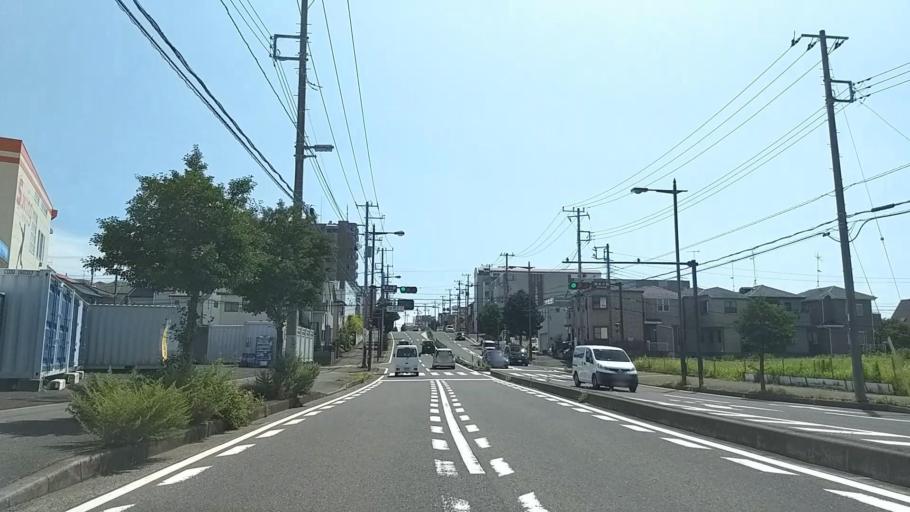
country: JP
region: Kanagawa
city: Fujisawa
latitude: 35.3563
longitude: 139.5037
